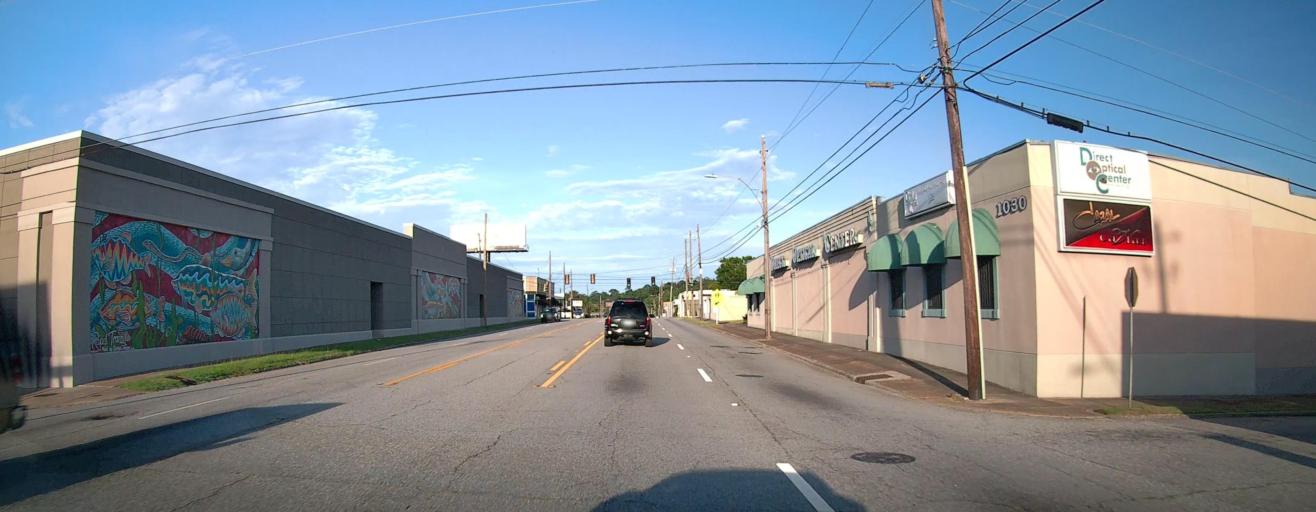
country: US
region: Georgia
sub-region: Muscogee County
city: Columbus
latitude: 32.4704
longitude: -84.9784
